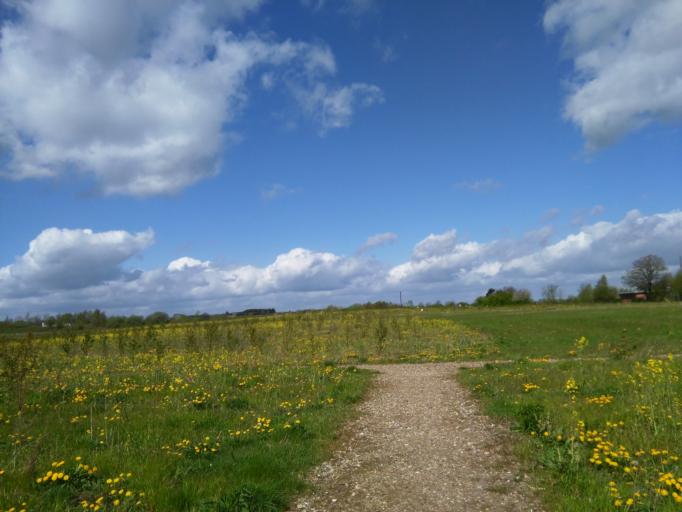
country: DK
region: Central Jutland
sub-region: Arhus Kommune
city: Malling
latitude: 56.0485
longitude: 10.1962
